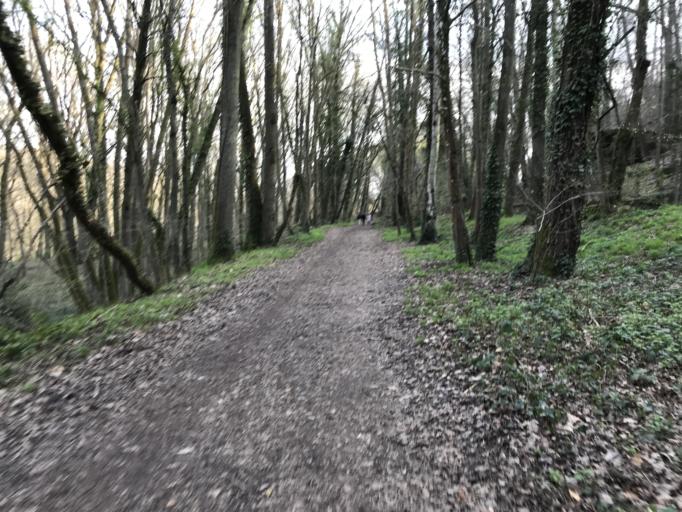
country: FR
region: Ile-de-France
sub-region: Departement de l'Essonne
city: Les Molieres
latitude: 48.6928
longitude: 2.0601
